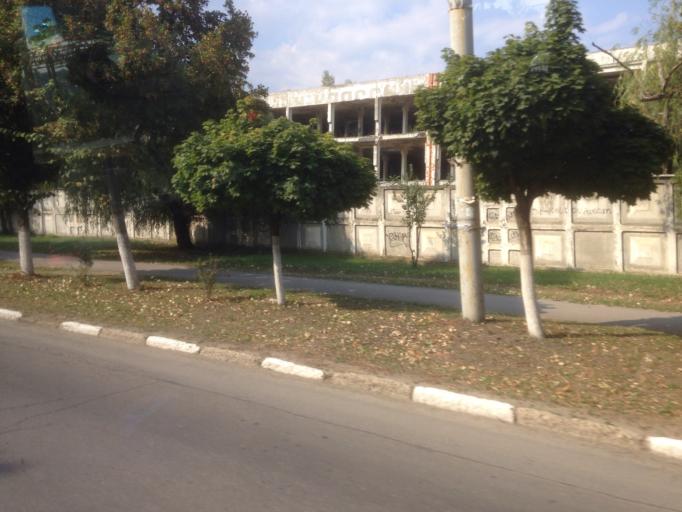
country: MD
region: Balti
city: Balti
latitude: 47.7596
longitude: 27.9407
